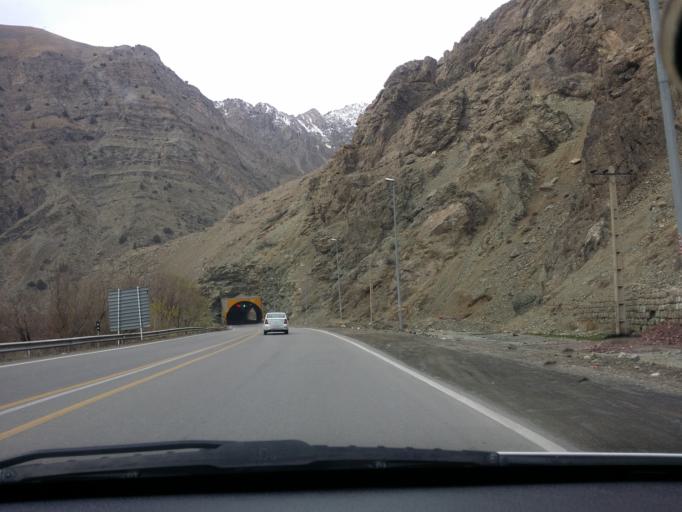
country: IR
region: Tehran
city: Tajrish
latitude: 36.0149
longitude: 51.2937
